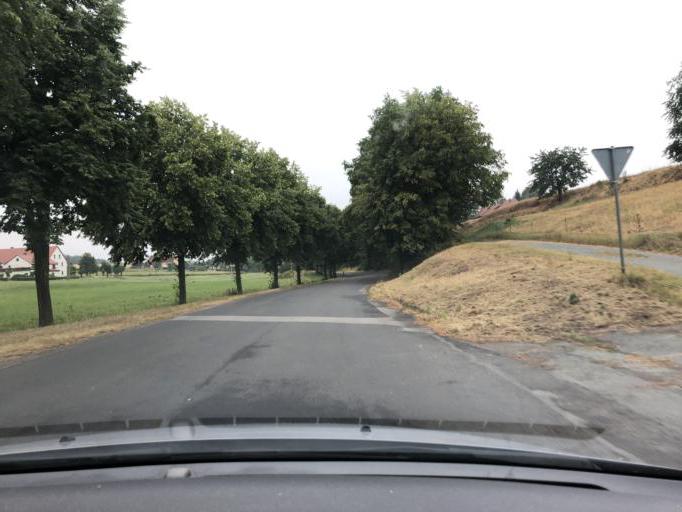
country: DE
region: Thuringia
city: Langenleuba-Niederhain
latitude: 50.9988
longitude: 12.6205
